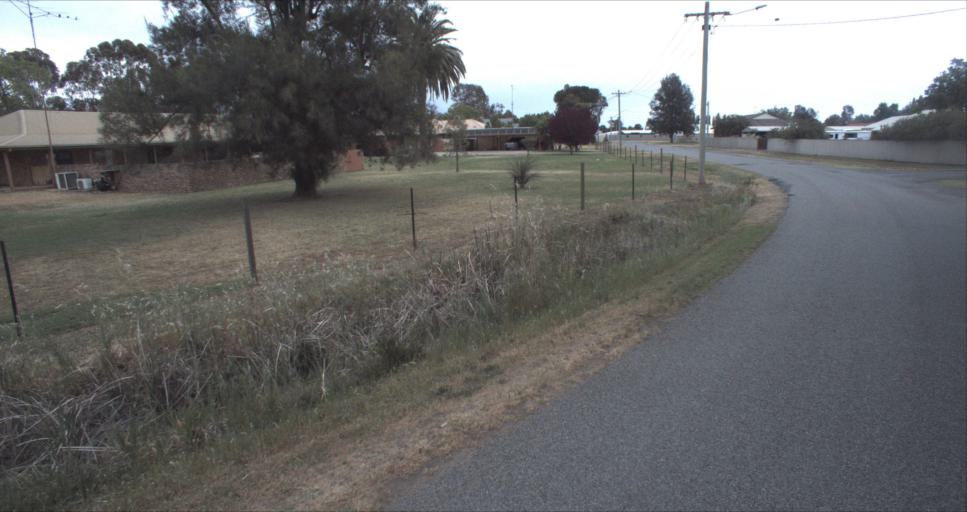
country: AU
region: New South Wales
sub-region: Leeton
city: Leeton
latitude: -34.5442
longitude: 146.4111
